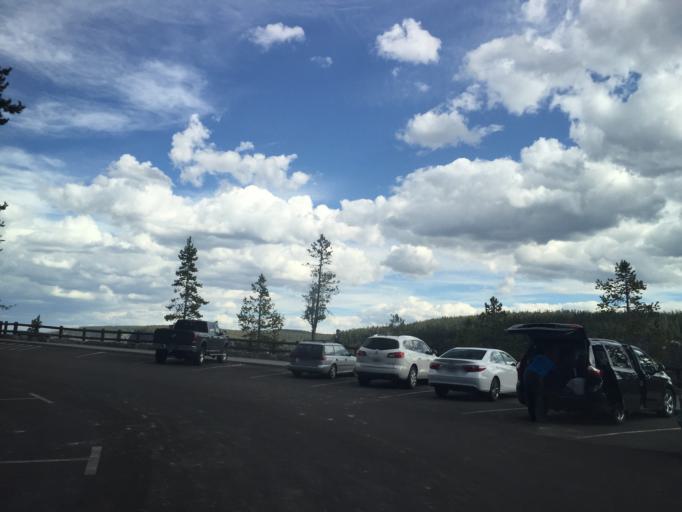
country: US
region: Montana
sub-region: Gallatin County
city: West Yellowstone
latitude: 44.7252
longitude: -110.4699
